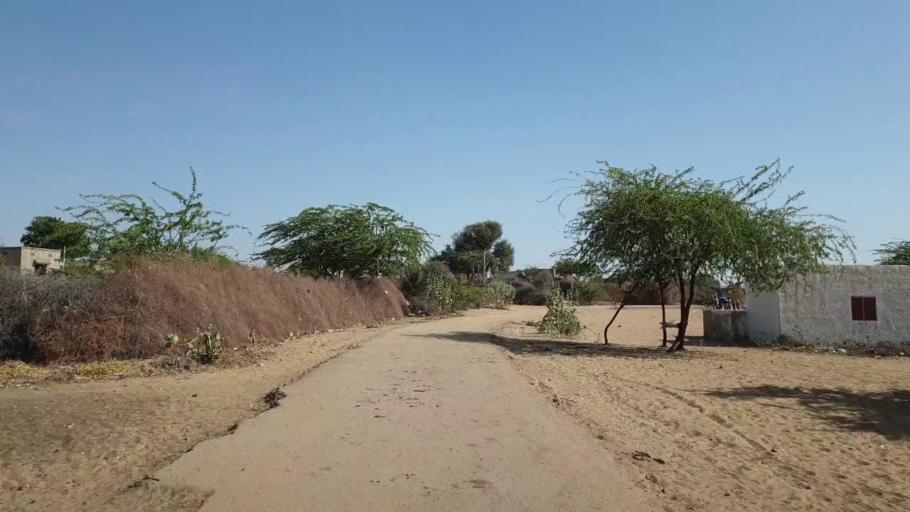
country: PK
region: Sindh
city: Umarkot
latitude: 25.1449
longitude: 70.0648
